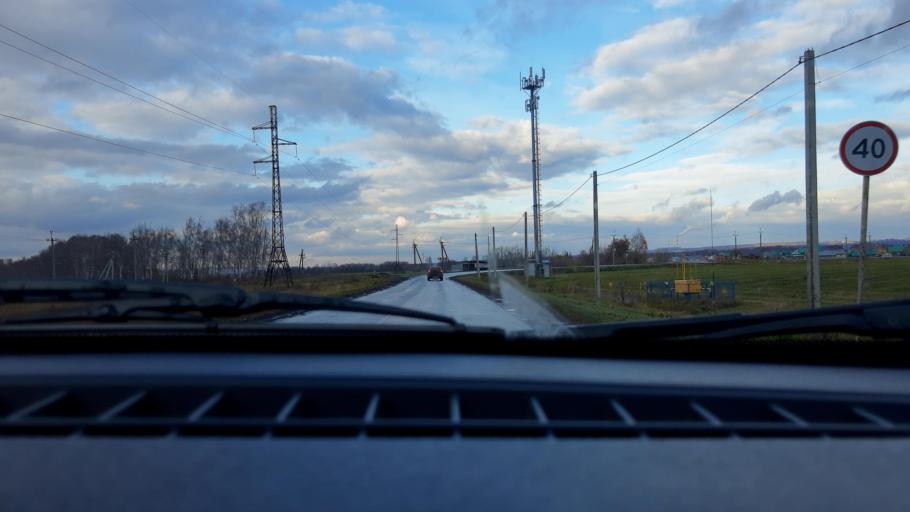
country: RU
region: Bashkortostan
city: Ufa
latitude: 54.8447
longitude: 56.0004
